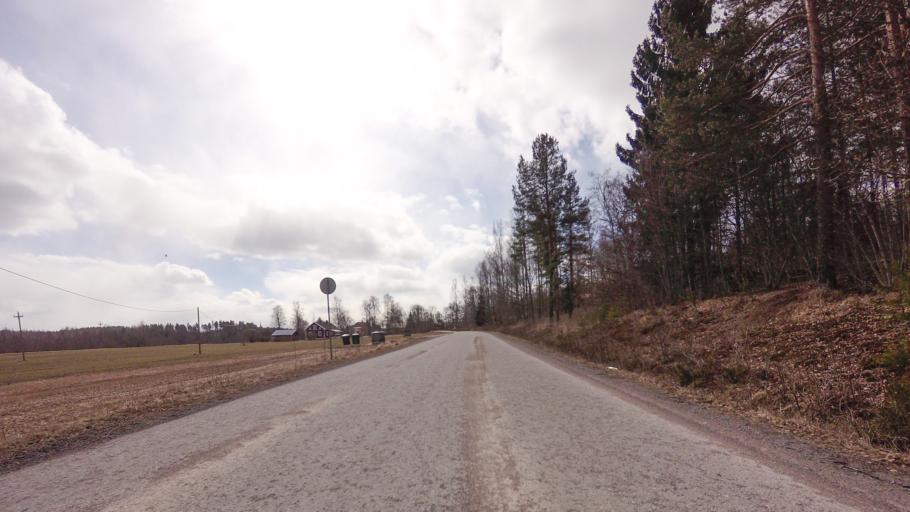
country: FI
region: Uusimaa
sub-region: Helsinki
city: Sammatti
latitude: 60.3016
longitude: 23.7568
